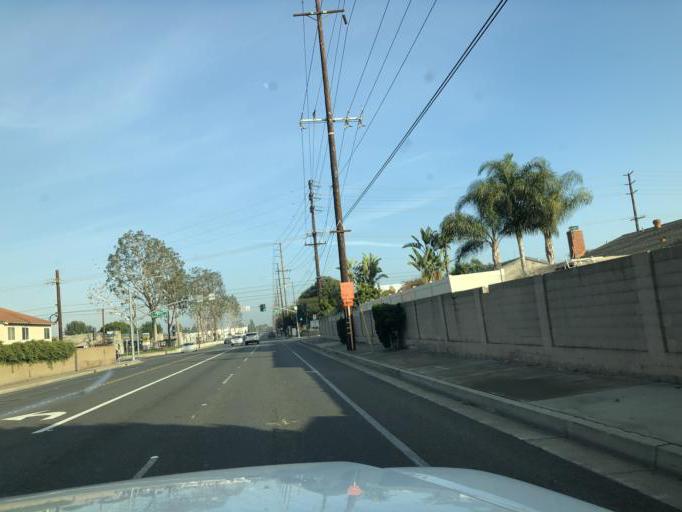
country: US
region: California
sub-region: Orange County
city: Fountain Valley
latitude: 33.6941
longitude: -117.9465
